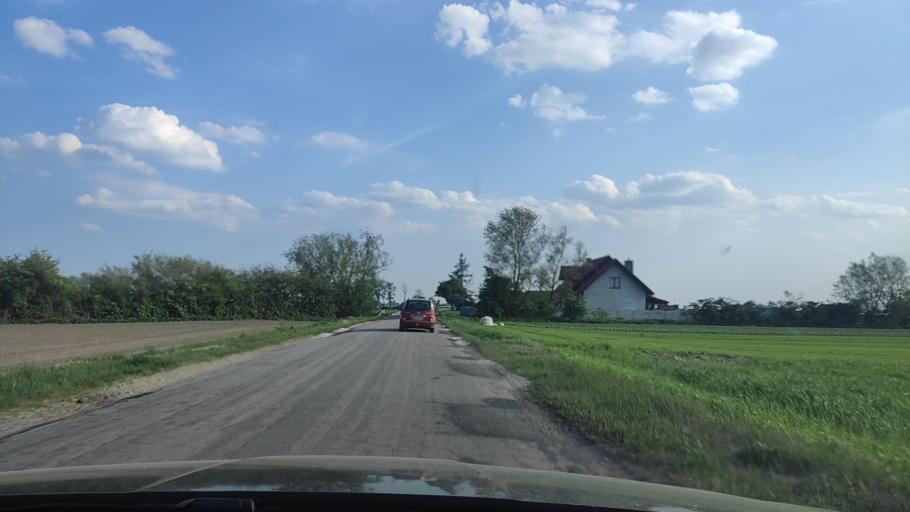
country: PL
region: Greater Poland Voivodeship
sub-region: Powiat poznanski
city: Kleszczewo
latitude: 52.3720
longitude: 17.1673
